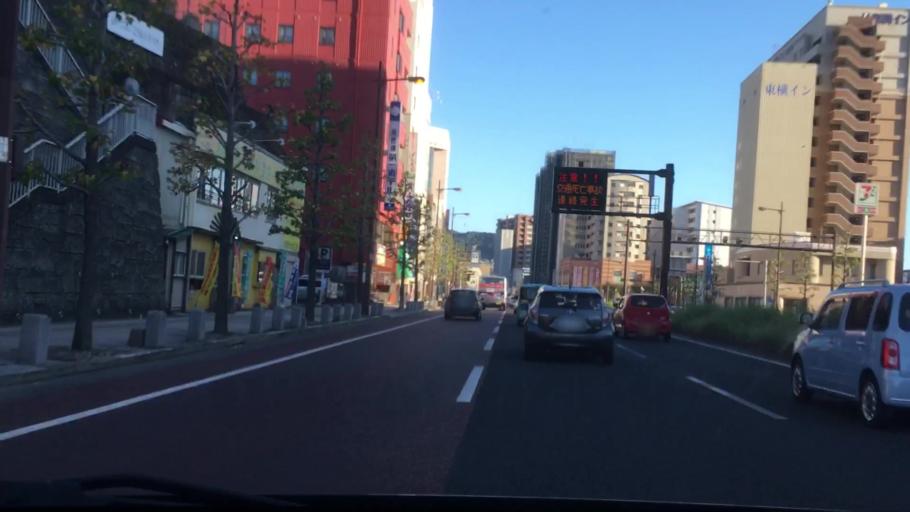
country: JP
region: Nagasaki
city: Sasebo
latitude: 33.1659
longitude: 129.7255
